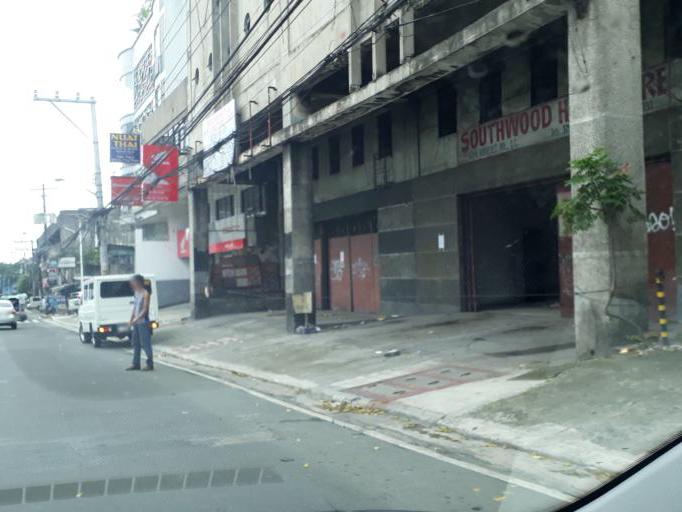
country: PH
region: Calabarzon
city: Del Monte
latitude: 14.6390
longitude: 121.0168
